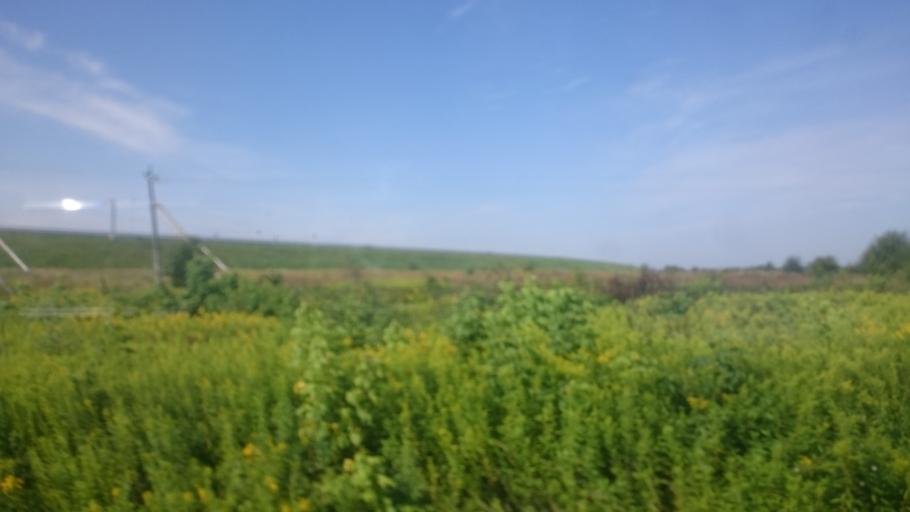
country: RU
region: Kaliningrad
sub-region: Zelenogradskiy Rayon
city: Zelenogradsk
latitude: 54.9151
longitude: 20.4912
